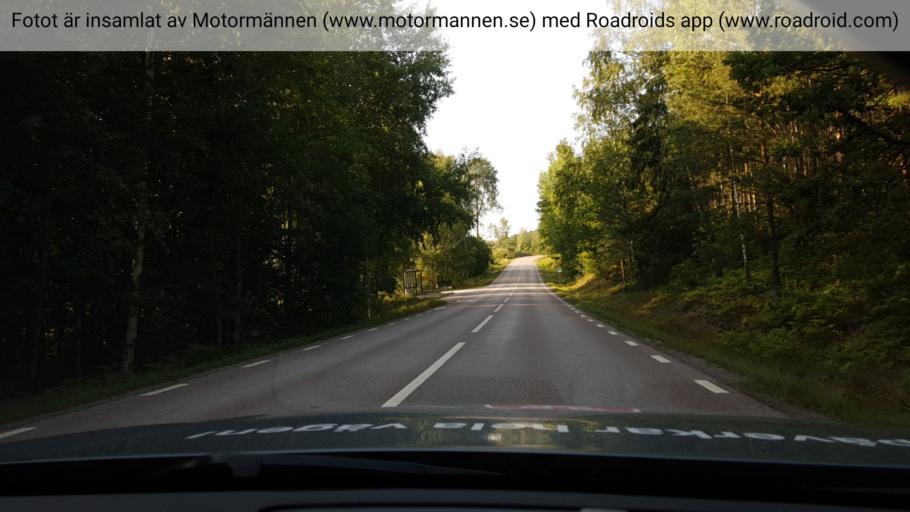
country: SE
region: Soedermanland
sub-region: Strangnas Kommun
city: Mariefred
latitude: 59.1887
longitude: 17.1862
